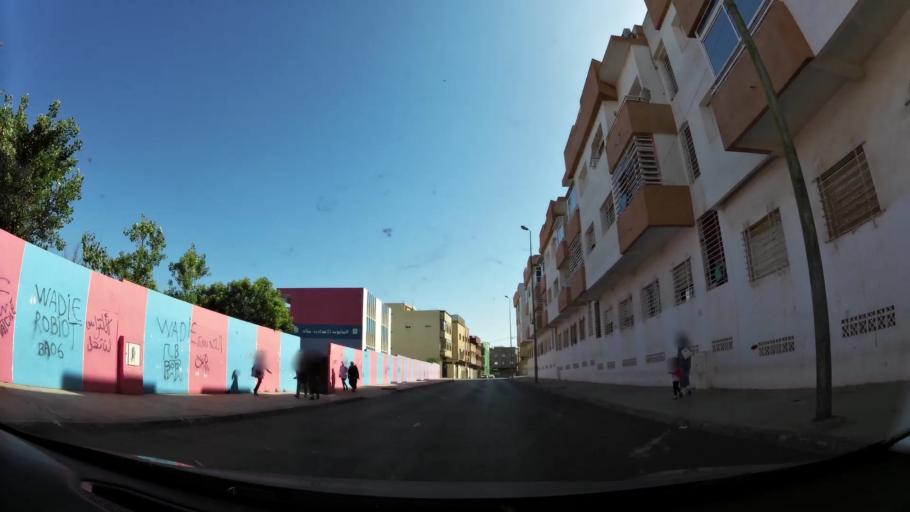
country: MA
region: Rabat-Sale-Zemmour-Zaer
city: Sale
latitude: 34.0696
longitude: -6.7954
